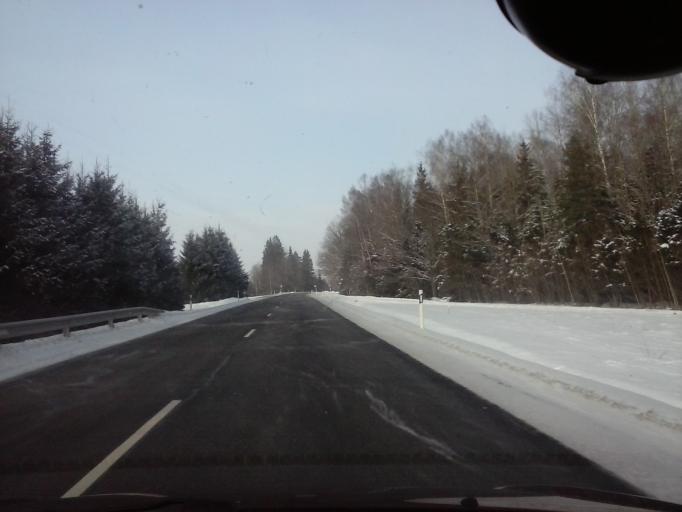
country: EE
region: Viljandimaa
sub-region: Abja vald
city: Abja-Paluoja
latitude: 58.3053
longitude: 25.2993
